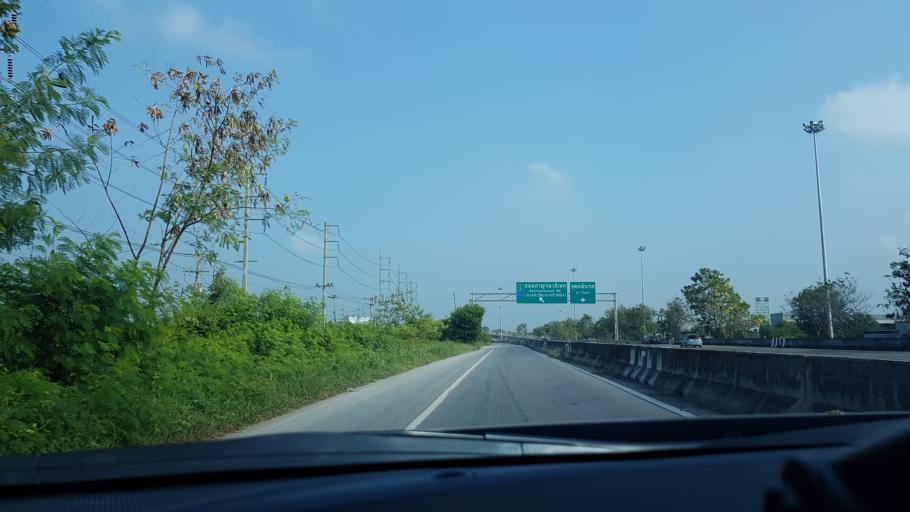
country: TH
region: Phra Nakhon Si Ayutthaya
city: Bang Pa-in
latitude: 14.1508
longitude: 100.5687
